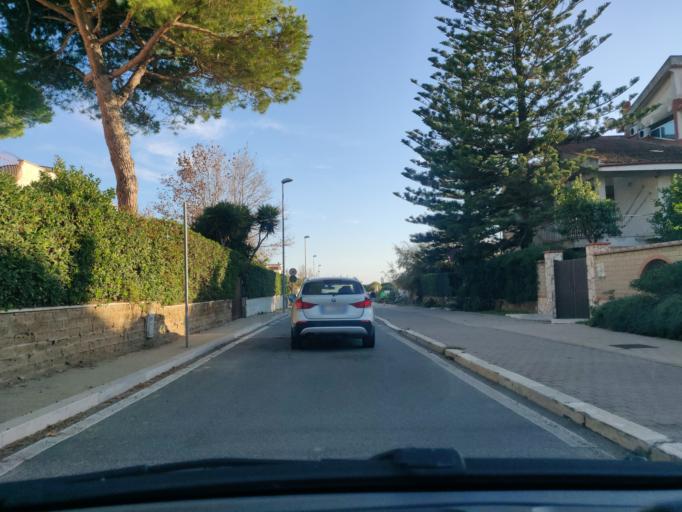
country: IT
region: Latium
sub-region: Citta metropolitana di Roma Capitale
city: Santa Marinella
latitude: 42.0318
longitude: 11.8344
